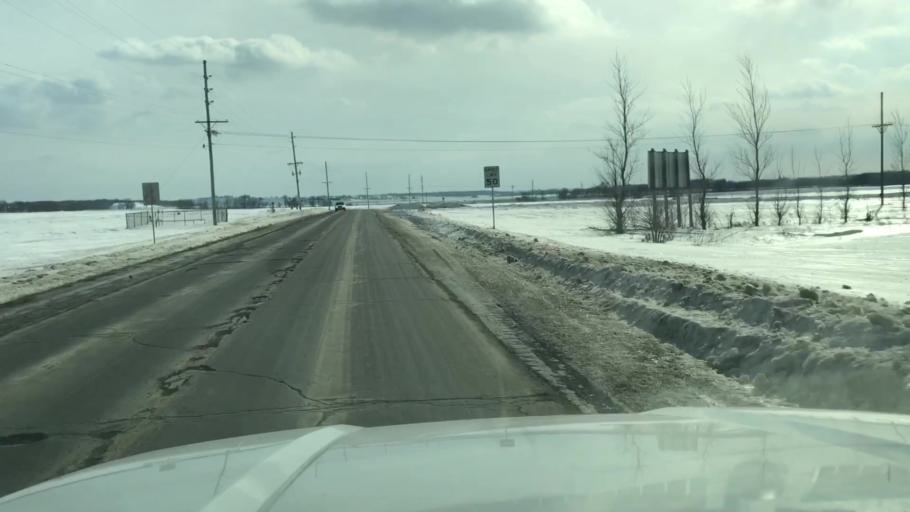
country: US
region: Missouri
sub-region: Gentry County
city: Stanberry
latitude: 40.3476
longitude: -94.6734
